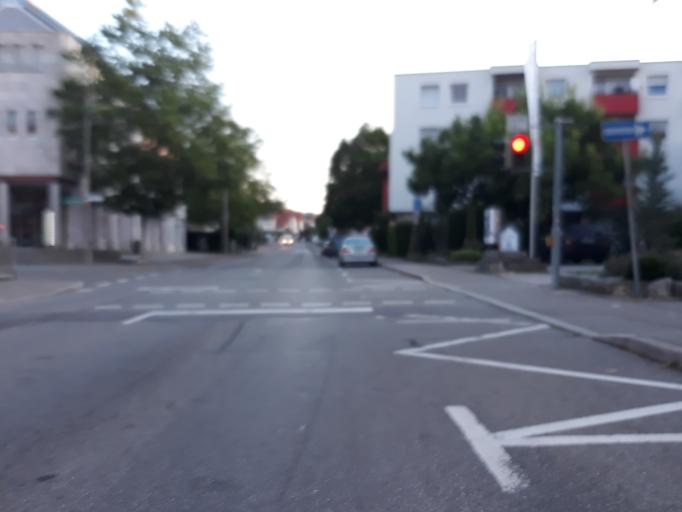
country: DE
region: Baden-Wuerttemberg
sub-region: Regierungsbezirk Stuttgart
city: Schonaich
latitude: 48.6616
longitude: 9.0594
